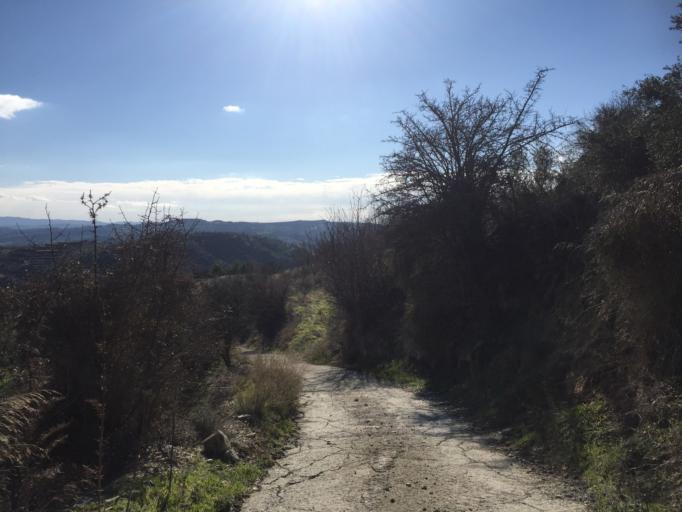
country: CY
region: Pafos
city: Mesogi
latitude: 34.8374
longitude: 32.5111
